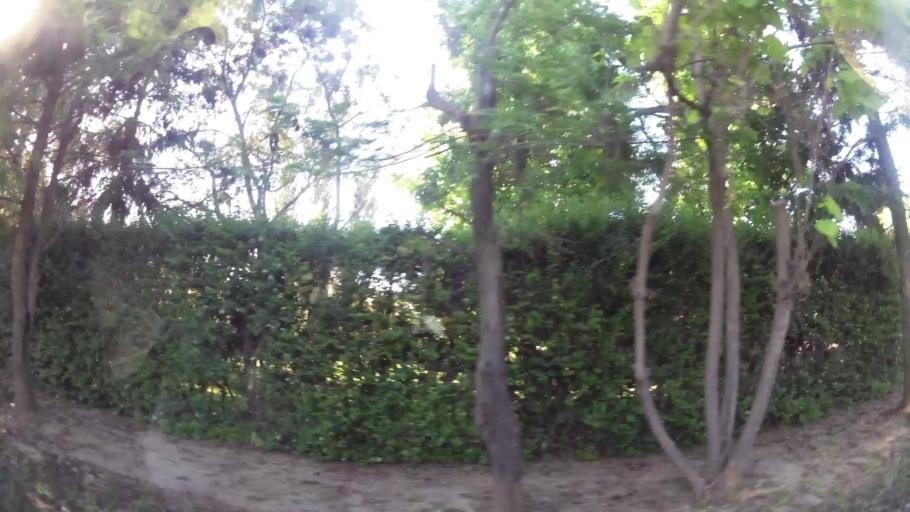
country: CL
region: Santiago Metropolitan
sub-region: Provincia de Maipo
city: San Bernardo
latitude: -33.6438
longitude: -70.6867
